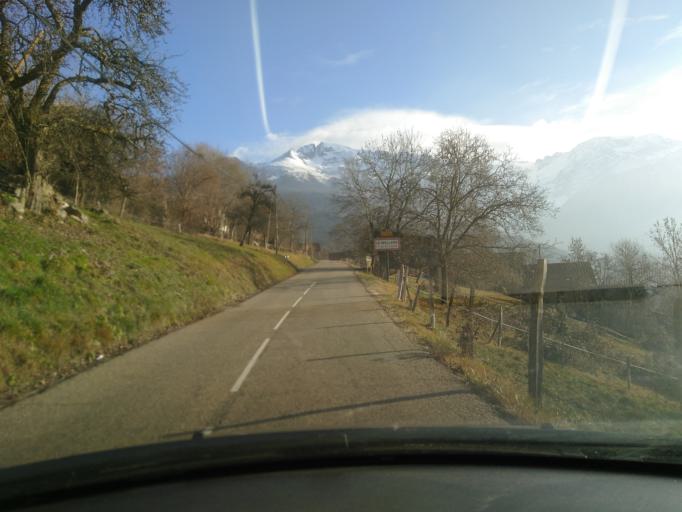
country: FR
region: Rhone-Alpes
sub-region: Departement de l'Isere
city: Froges
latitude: 45.2368
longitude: 5.9312
